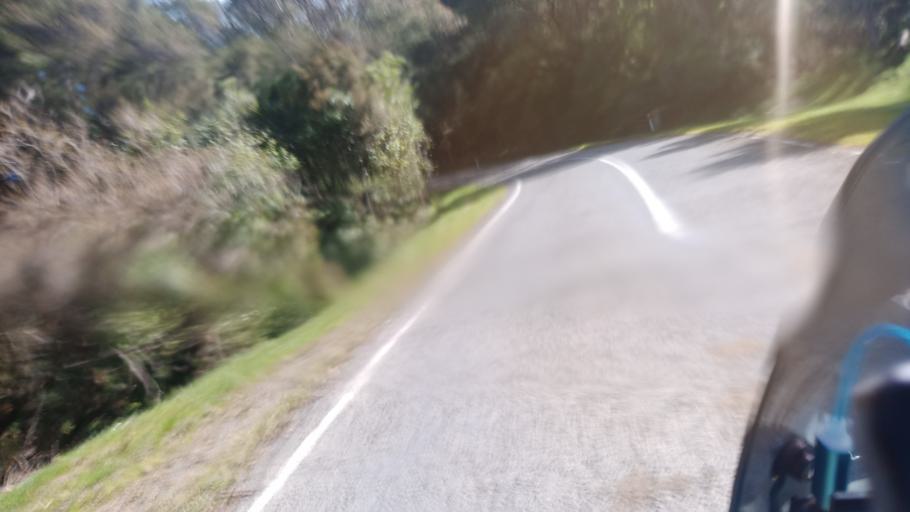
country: NZ
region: Gisborne
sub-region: Gisborne District
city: Gisborne
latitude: -37.8639
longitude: 178.2366
